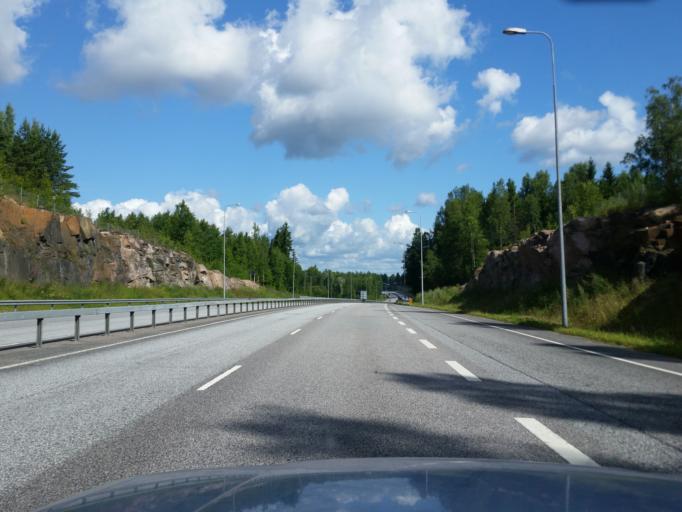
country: FI
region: Uusimaa
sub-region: Helsinki
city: Vihti
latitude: 60.3064
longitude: 24.3510
